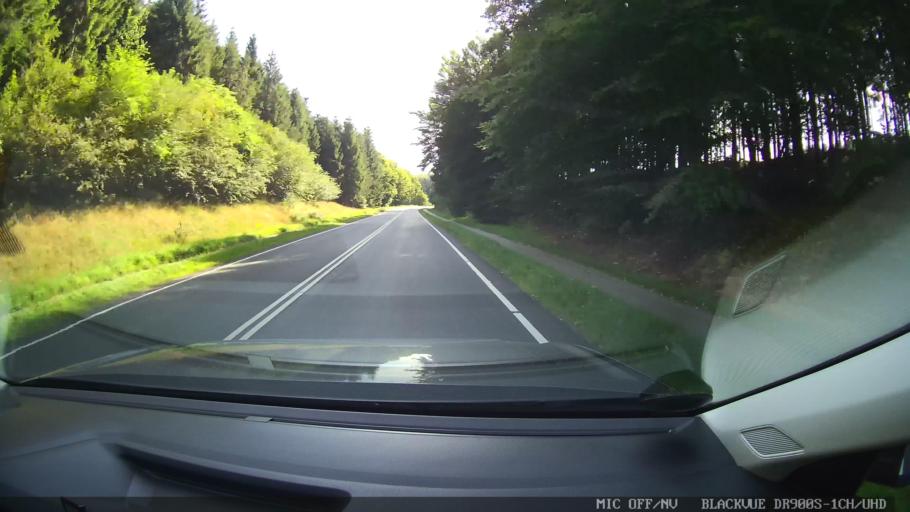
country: DK
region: North Denmark
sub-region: Mariagerfjord Kommune
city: Arden
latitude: 56.7786
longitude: 9.7641
